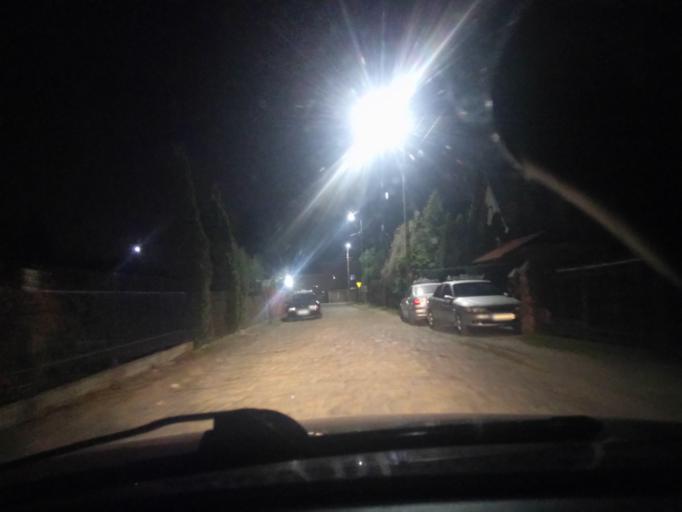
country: PL
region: Warmian-Masurian Voivodeship
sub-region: Powiat elblaski
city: Elblag
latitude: 54.1800
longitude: 19.4118
